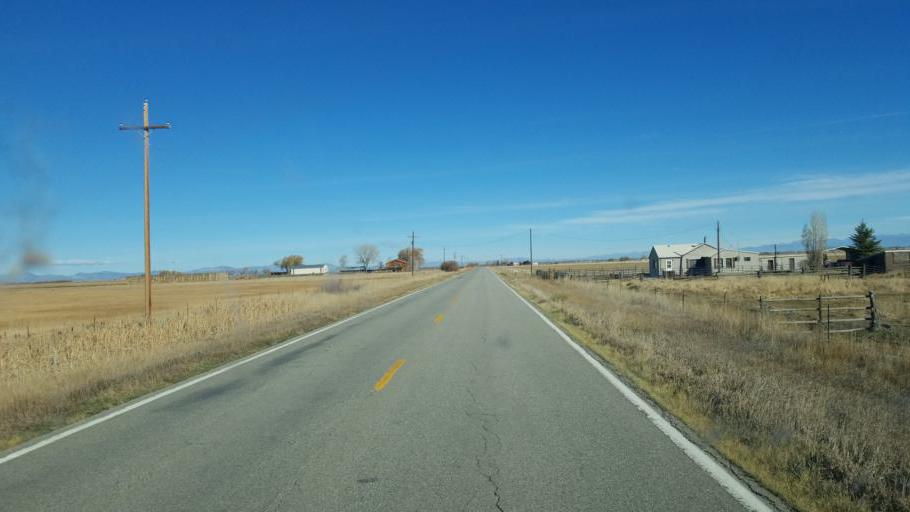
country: US
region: Colorado
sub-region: Rio Grande County
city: Monte Vista
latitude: 37.5044
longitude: -106.1491
